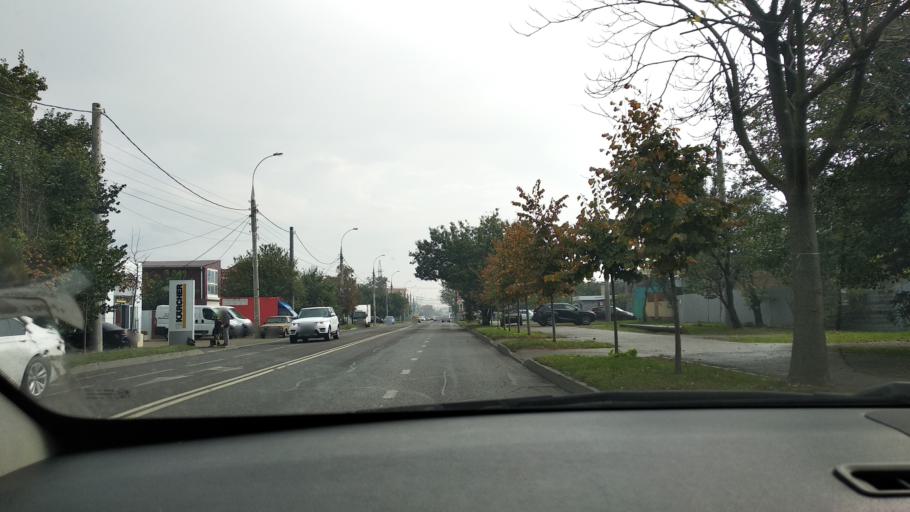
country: RU
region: Krasnodarskiy
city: Krasnodar
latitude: 45.0278
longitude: 39.0227
